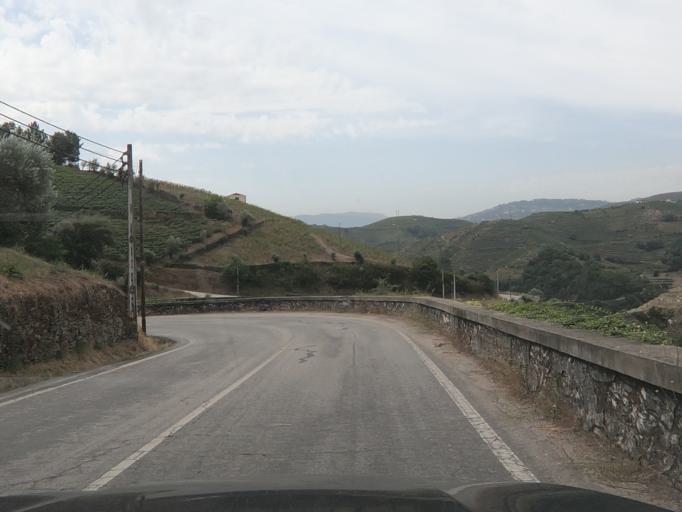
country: PT
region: Vila Real
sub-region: Santa Marta de Penaguiao
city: Santa Marta de Penaguiao
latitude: 41.2322
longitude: -7.7644
